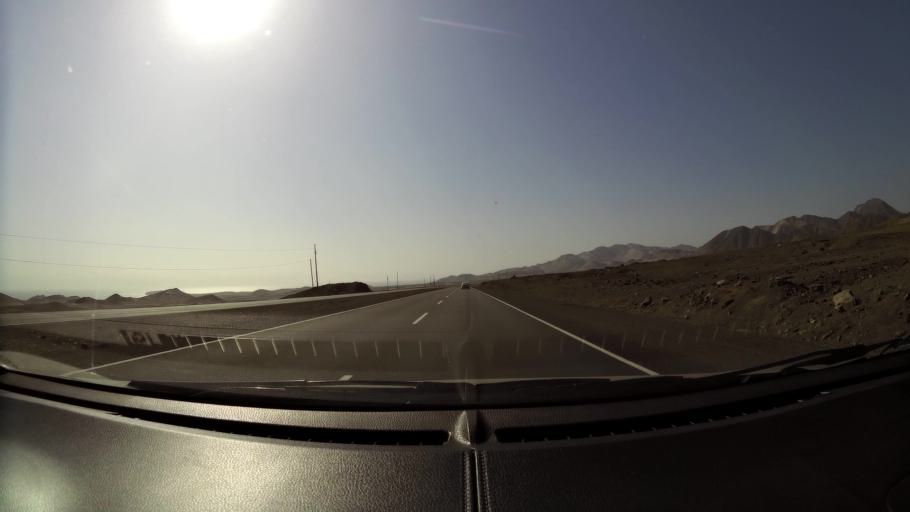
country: PE
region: Ancash
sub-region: Provincia de Huarmey
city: La Caleta Culebras
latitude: -9.8861
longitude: -78.2117
